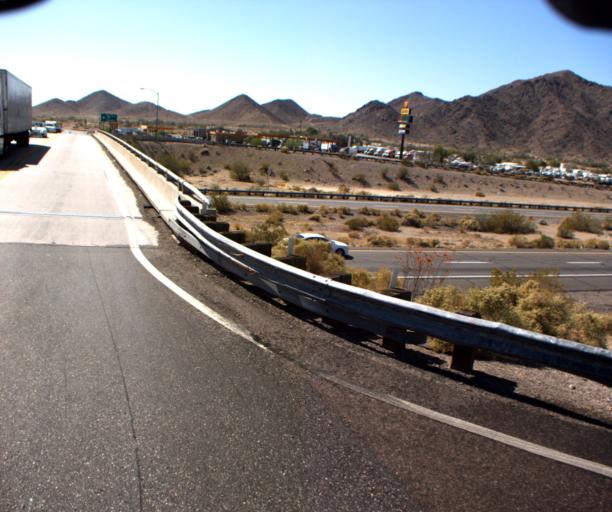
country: US
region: Arizona
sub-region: La Paz County
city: Quartzsite
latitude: 33.6602
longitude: -114.2410
